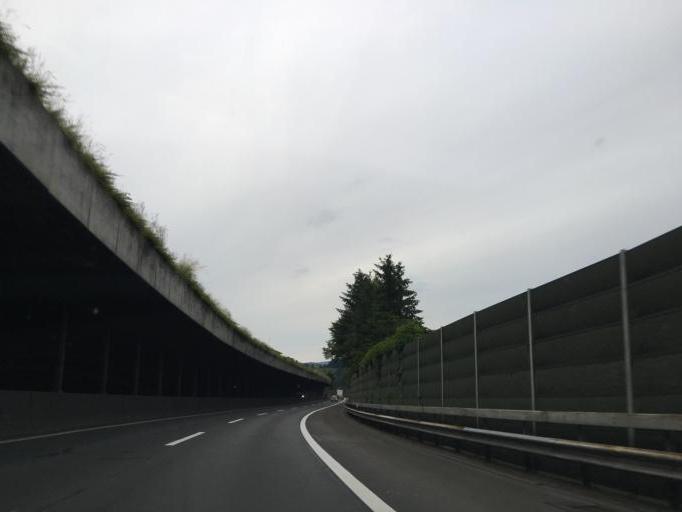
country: CH
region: Nidwalden
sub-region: Nidwalden
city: Hergiswil
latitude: 46.9935
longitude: 8.3080
